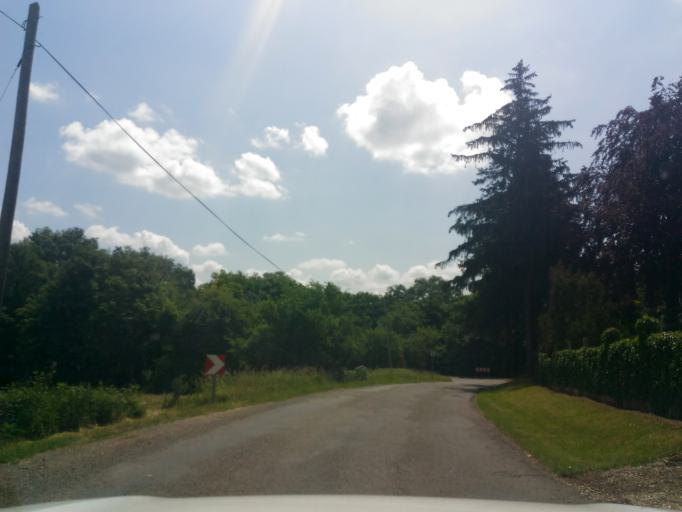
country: HU
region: Baranya
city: Pecs
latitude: 46.1315
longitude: 18.2365
